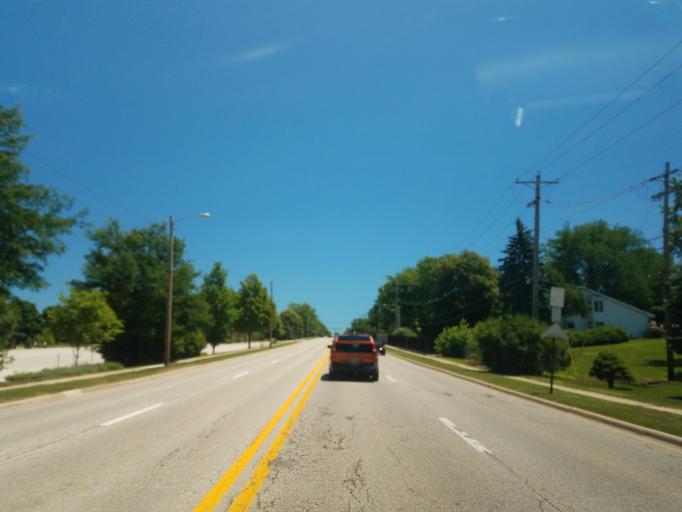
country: US
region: Illinois
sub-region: McLean County
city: Normal
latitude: 40.5103
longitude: -88.9728
